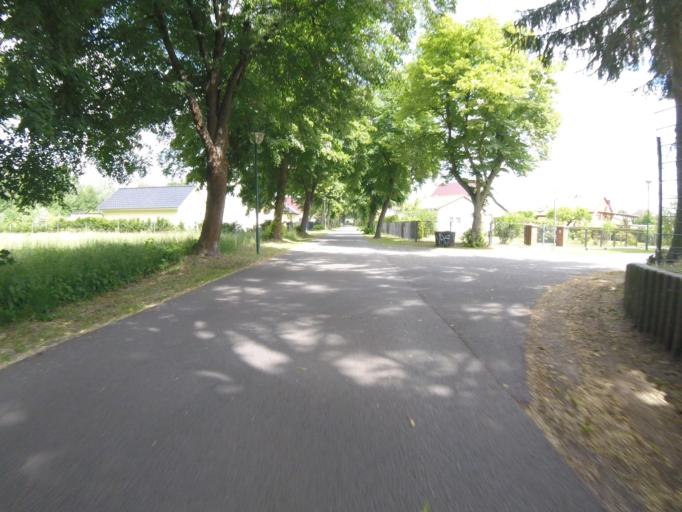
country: DE
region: Brandenburg
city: Halbe
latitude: 52.1094
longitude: 13.6947
